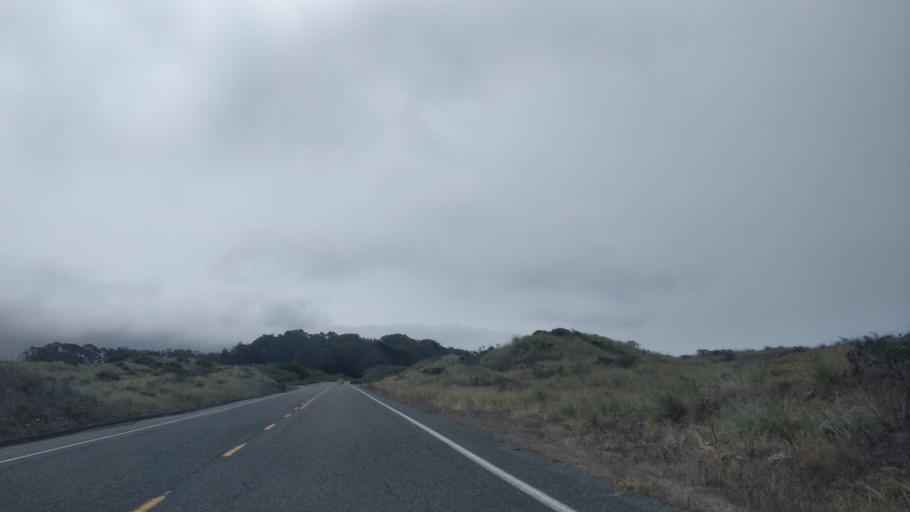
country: US
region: California
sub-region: Humboldt County
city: Bayview
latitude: 40.7844
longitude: -124.2069
